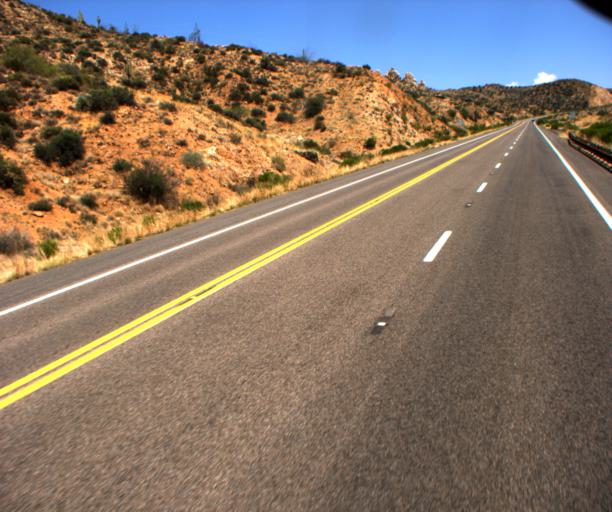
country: US
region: Arizona
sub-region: Gila County
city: Miami
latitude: 33.5480
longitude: -110.9450
